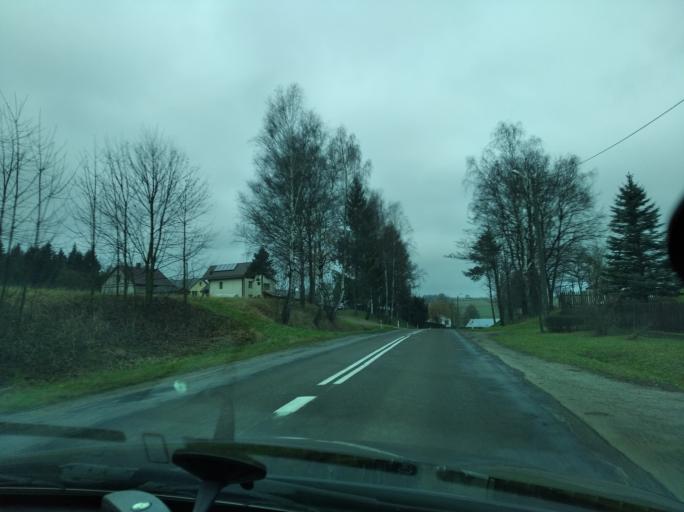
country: PL
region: Subcarpathian Voivodeship
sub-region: Powiat przeworski
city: Jawornik Polski
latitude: 49.8669
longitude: 22.2457
